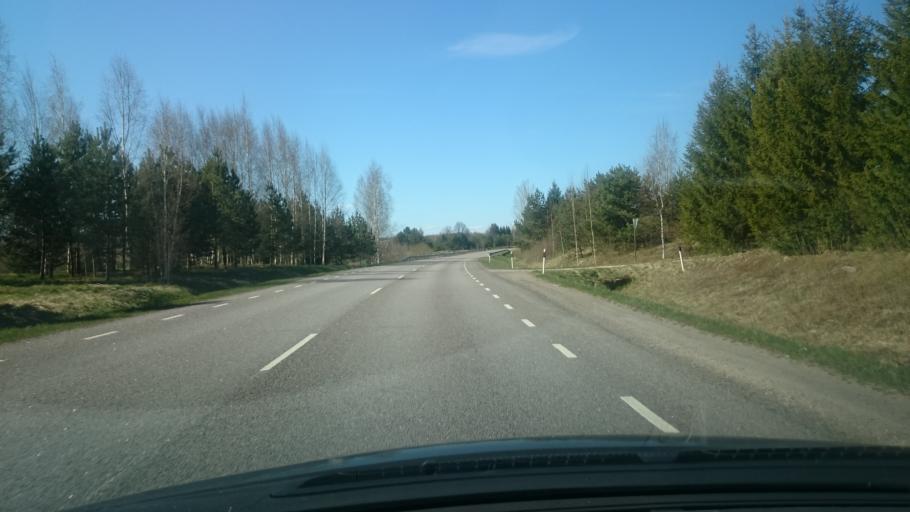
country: EE
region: Polvamaa
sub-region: Polva linn
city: Polva
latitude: 58.2475
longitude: 27.0030
